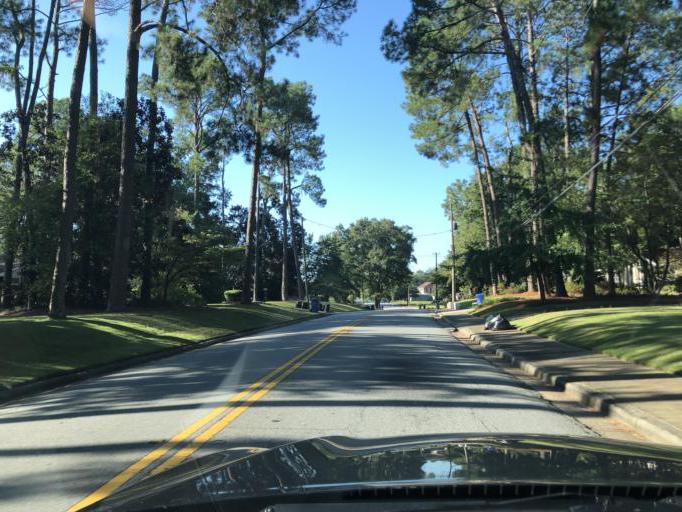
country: US
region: Georgia
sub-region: Muscogee County
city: Columbus
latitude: 32.4859
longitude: -84.9457
